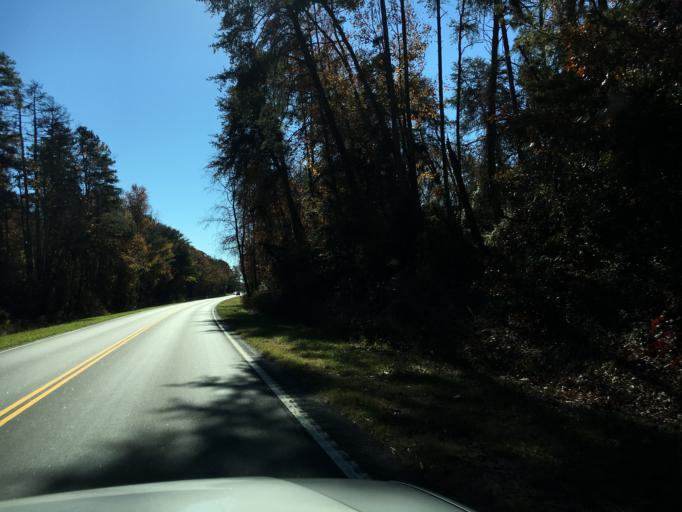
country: US
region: Georgia
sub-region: Hart County
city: Hartwell
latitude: 34.3798
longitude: -82.8112
